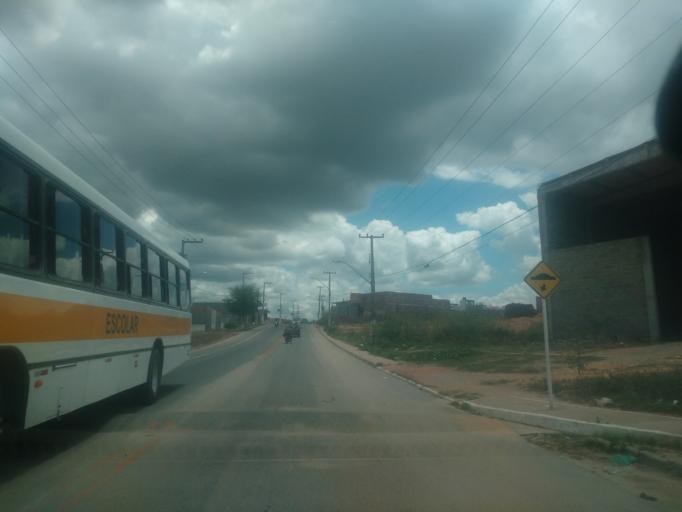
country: BR
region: Alagoas
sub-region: Uniao Dos Palmares
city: Uniao dos Palmares
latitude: -9.1532
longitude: -36.0189
